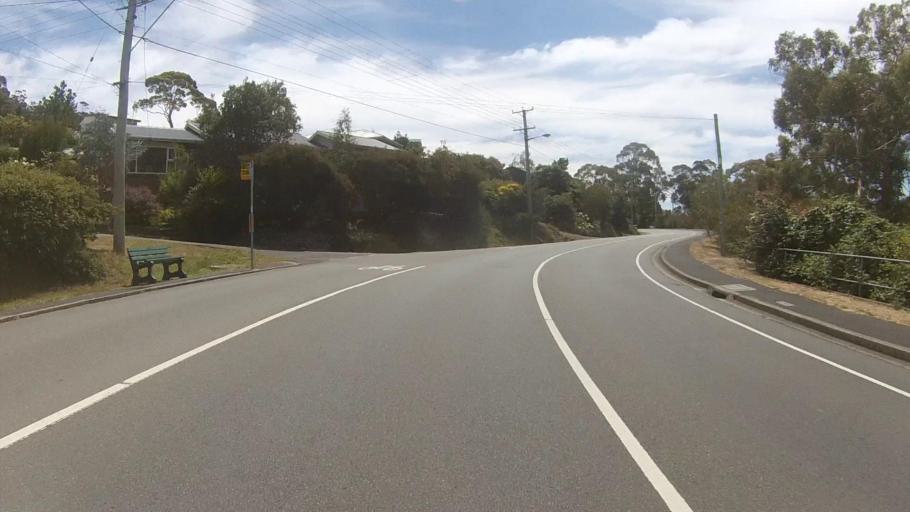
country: AU
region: Tasmania
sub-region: Kingborough
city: Taroona
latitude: -42.9412
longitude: 147.3526
